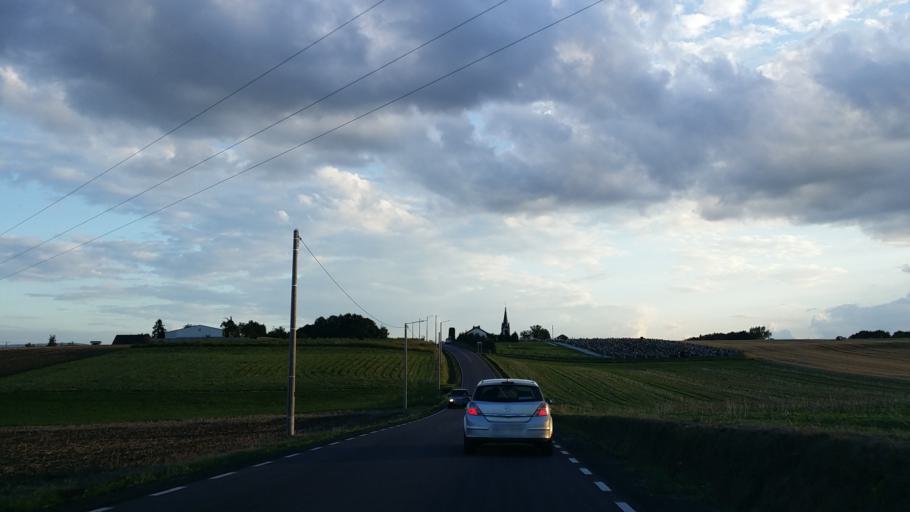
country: PL
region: Lesser Poland Voivodeship
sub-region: Powiat oswiecimski
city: Osiek
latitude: 49.9585
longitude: 19.2718
